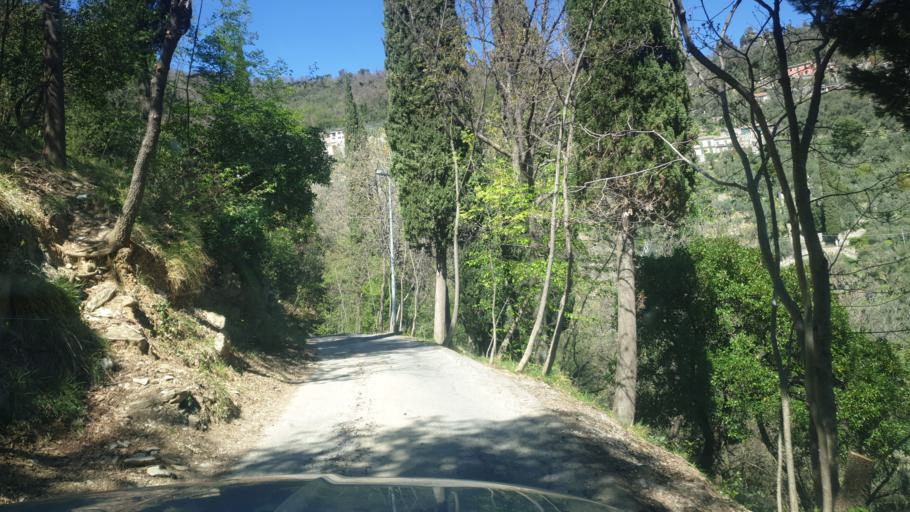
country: IT
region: Liguria
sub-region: Provincia di Genova
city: Recco
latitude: 44.3699
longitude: 9.1435
